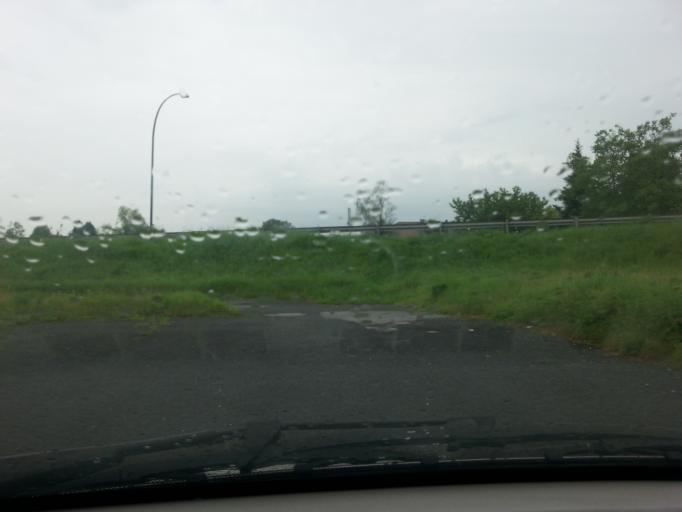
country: IT
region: Piedmont
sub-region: Provincia di Torino
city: Alpignano
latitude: 45.1032
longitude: 7.5101
